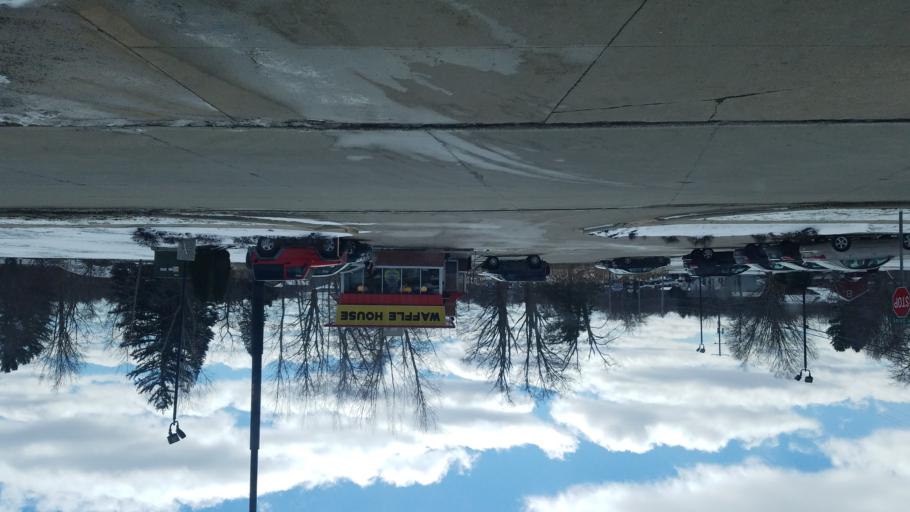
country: US
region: Ohio
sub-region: Ashtabula County
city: Geneva
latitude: 41.7844
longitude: -80.8553
